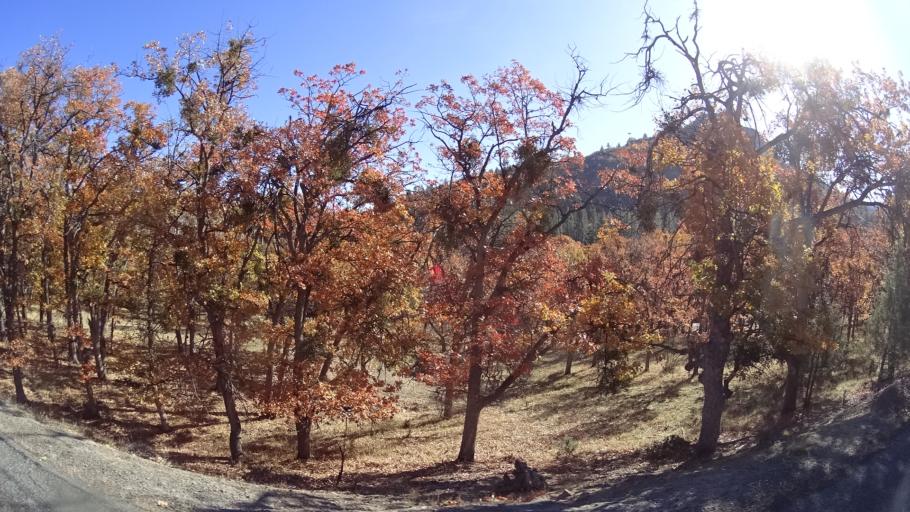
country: US
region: California
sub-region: Siskiyou County
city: Montague
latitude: 41.9739
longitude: -122.3031
